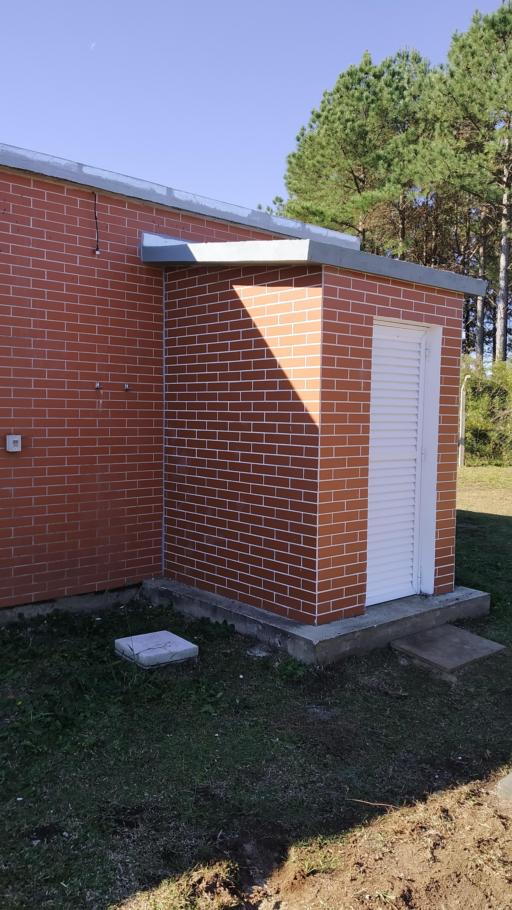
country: BR
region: Santa Catarina
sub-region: Curitibanos
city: Curitibanos
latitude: -27.2845
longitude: -50.5333
